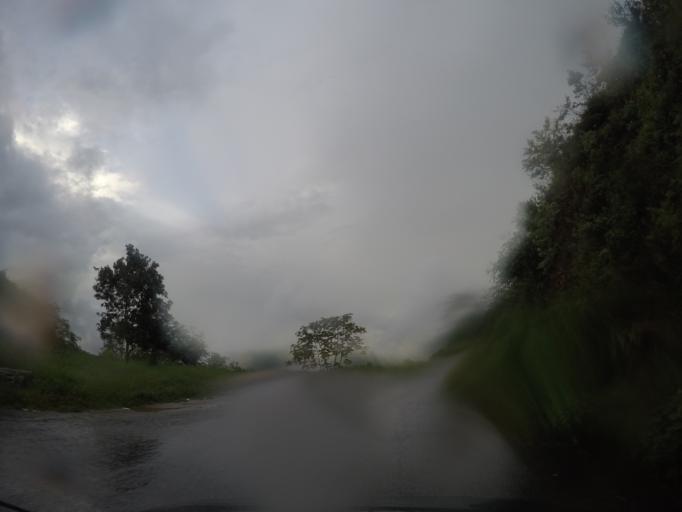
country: MX
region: Oaxaca
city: San Gabriel Mixtepec
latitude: 16.0643
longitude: -97.0753
